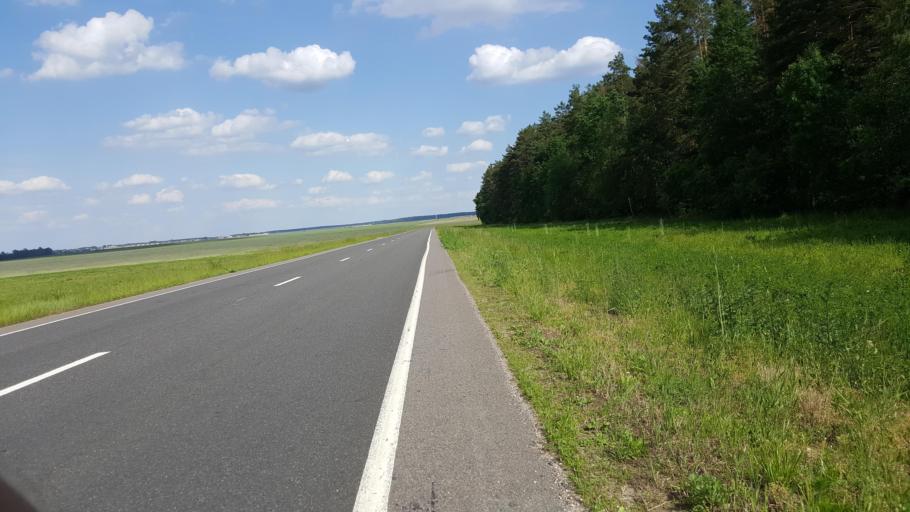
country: BY
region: Brest
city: Pruzhany
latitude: 52.5492
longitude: 24.1470
